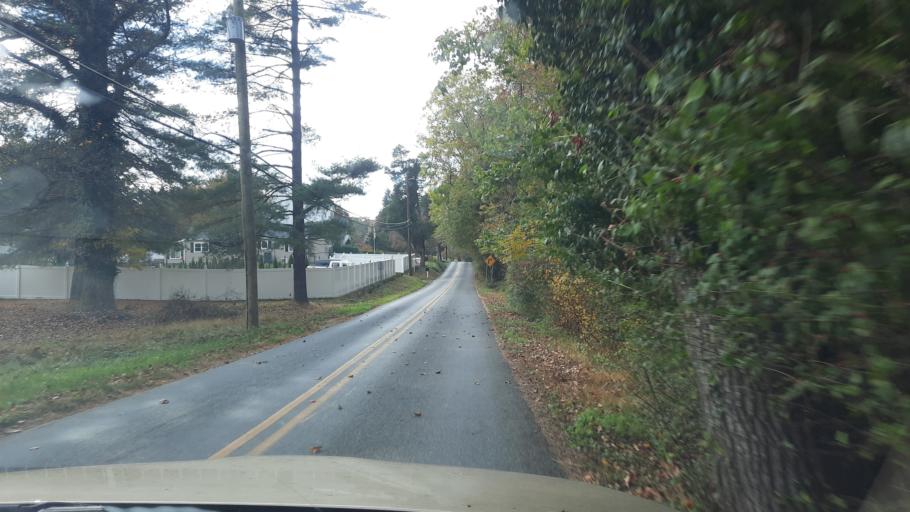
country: US
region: Maryland
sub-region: Montgomery County
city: Germantown
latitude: 39.1524
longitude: -77.2410
